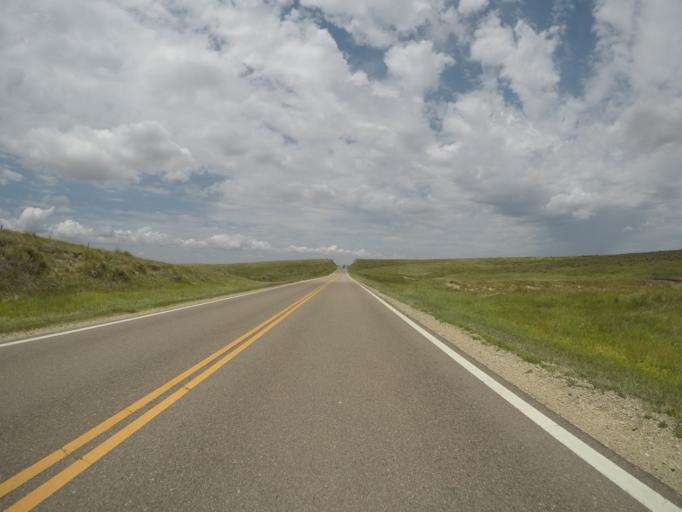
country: US
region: Kansas
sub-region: Rawlins County
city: Atwood
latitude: 39.7454
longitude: -101.0504
